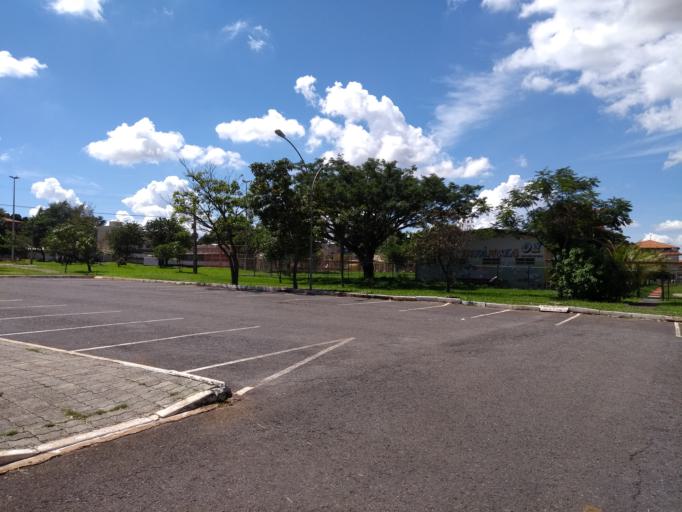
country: BR
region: Federal District
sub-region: Brasilia
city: Brasilia
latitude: -15.7843
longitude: -47.9354
